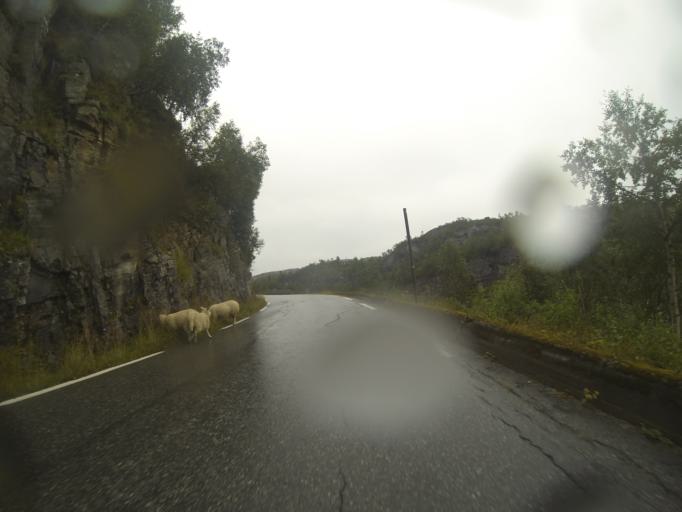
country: NO
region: Rogaland
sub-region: Sauda
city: Sauda
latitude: 59.7250
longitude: 6.5698
